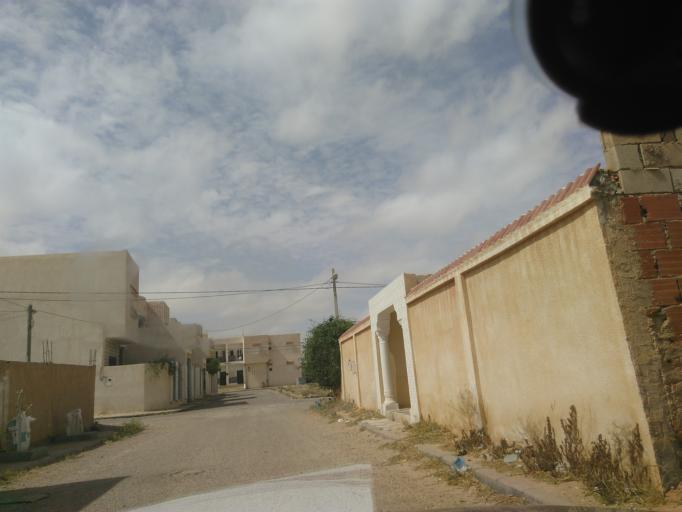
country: TN
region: Tataouine
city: Tataouine
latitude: 32.9547
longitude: 10.4668
